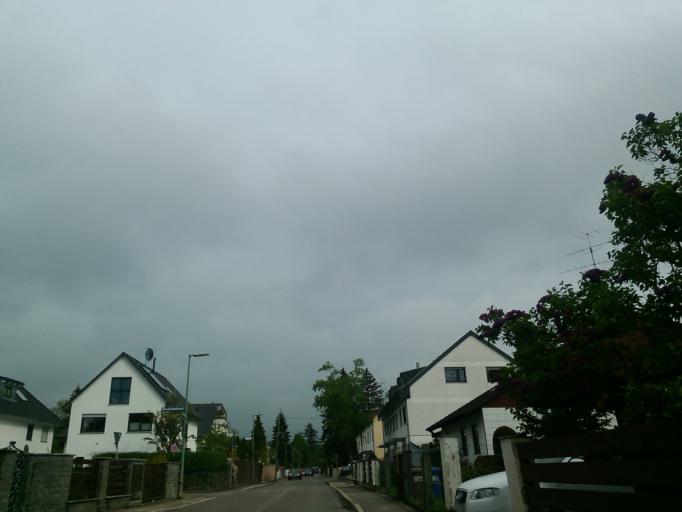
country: DE
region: Bavaria
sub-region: Upper Bavaria
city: Haar
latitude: 48.1141
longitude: 11.6876
